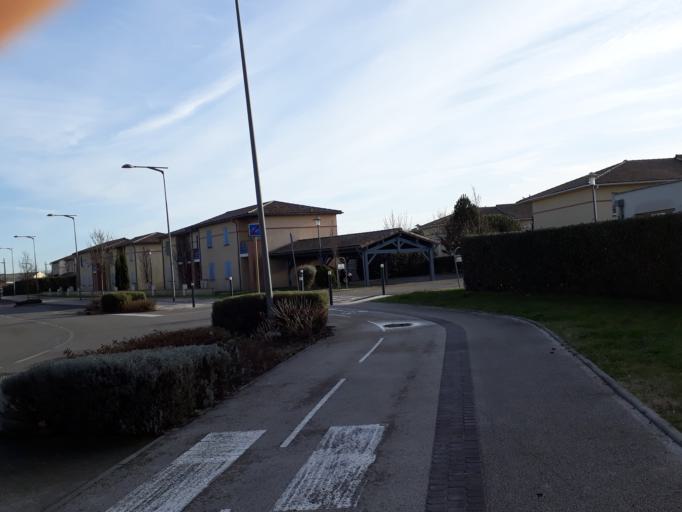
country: FR
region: Midi-Pyrenees
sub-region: Departement de la Haute-Garonne
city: Beauzelle
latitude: 43.6605
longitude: 1.3790
